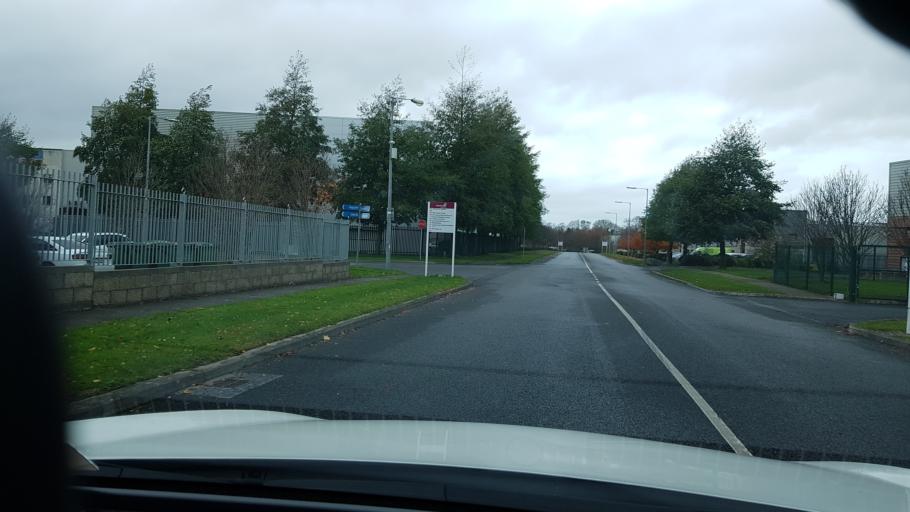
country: IE
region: Leinster
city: Castleknock
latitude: 53.3992
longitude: -6.3433
